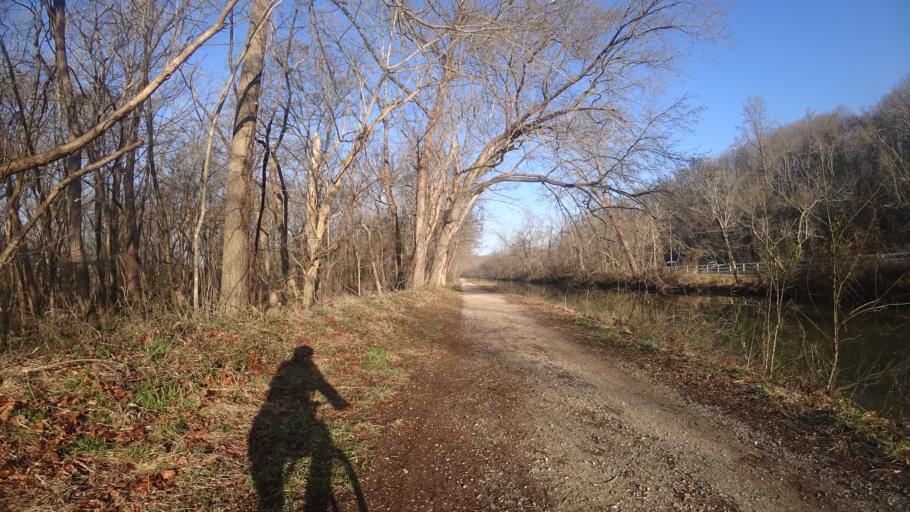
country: US
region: Maryland
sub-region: Montgomery County
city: Travilah
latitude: 39.0542
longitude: -77.2898
